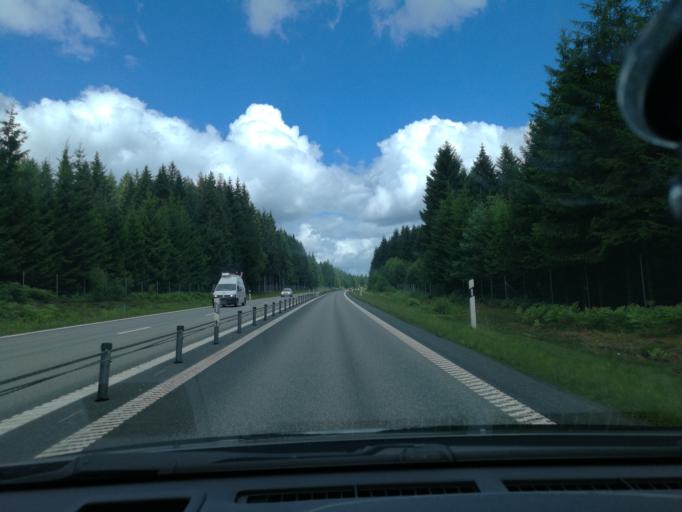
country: SE
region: Skane
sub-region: Hassleholms Kommun
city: Hassleholm
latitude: 56.1928
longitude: 13.8494
